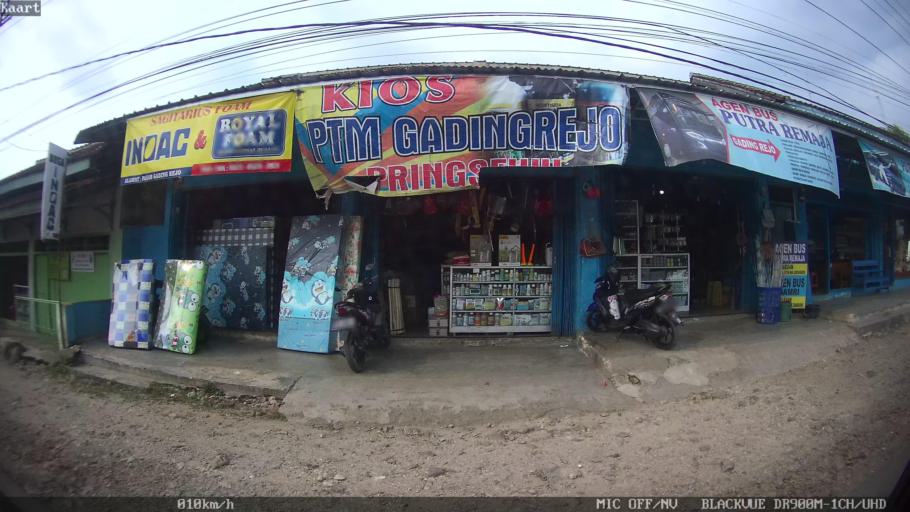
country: ID
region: Lampung
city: Gadingrejo
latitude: -5.3731
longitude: 105.0594
